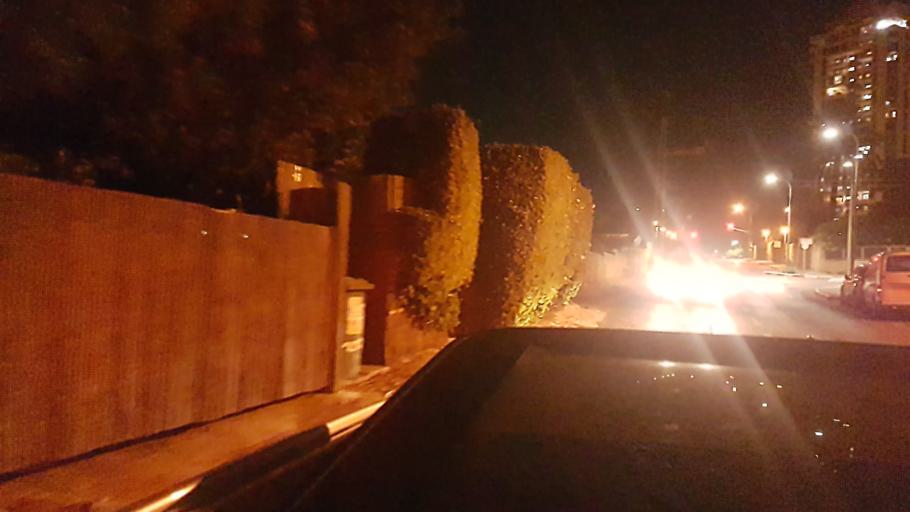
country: IL
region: Central District
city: Hod HaSharon
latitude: 32.1628
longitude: 34.8922
